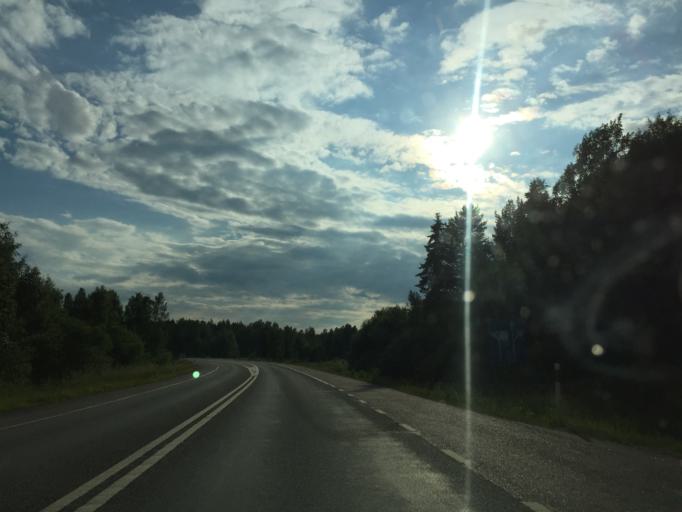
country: SE
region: Vaestmanland
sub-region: Arboga Kommun
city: Arboga
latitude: 59.3687
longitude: 15.7062
